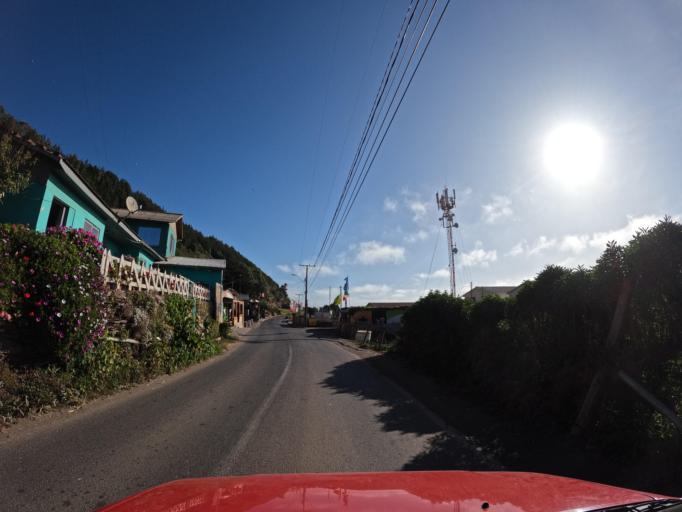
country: CL
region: Maule
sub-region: Provincia de Talca
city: Constitucion
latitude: -34.8902
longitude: -72.1738
